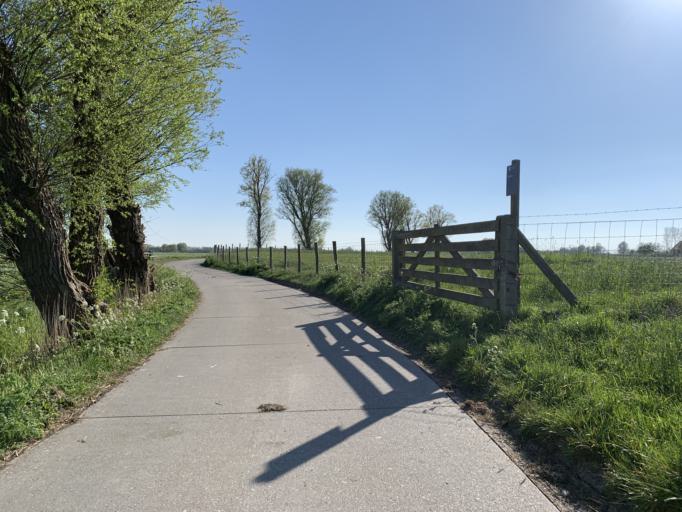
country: NL
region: Groningen
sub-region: Gemeente Winsum
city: Winsum
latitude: 53.2849
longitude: 6.5151
